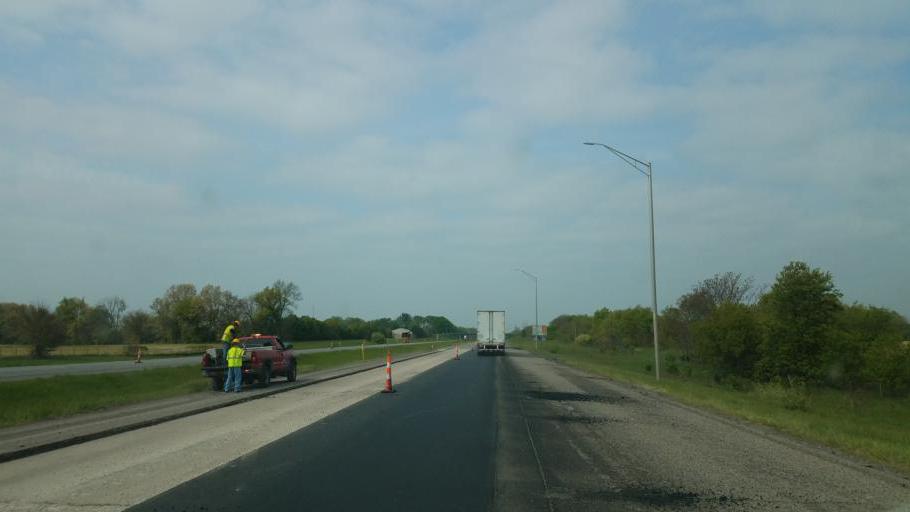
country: US
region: Indiana
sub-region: Saint Joseph County
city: Granger
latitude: 41.7287
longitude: -86.1476
